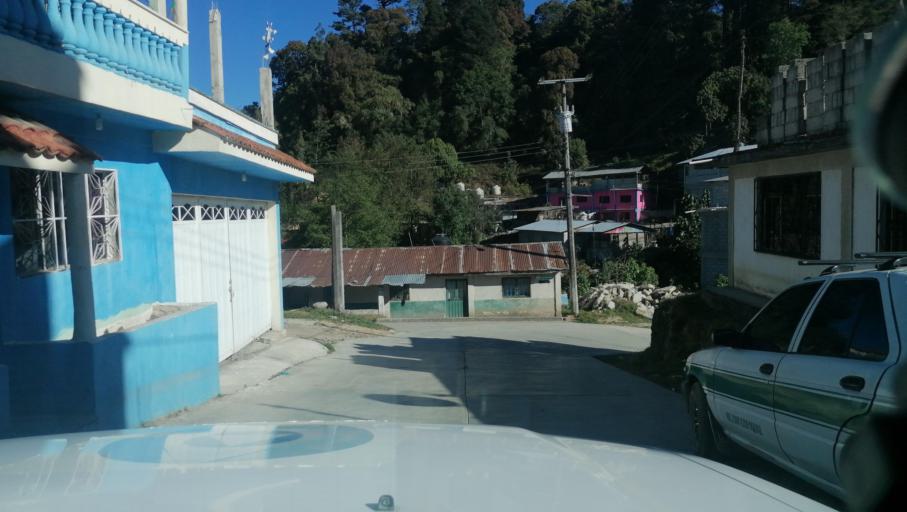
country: MX
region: Chiapas
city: Motozintla de Mendoza
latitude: 15.2596
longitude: -92.2137
